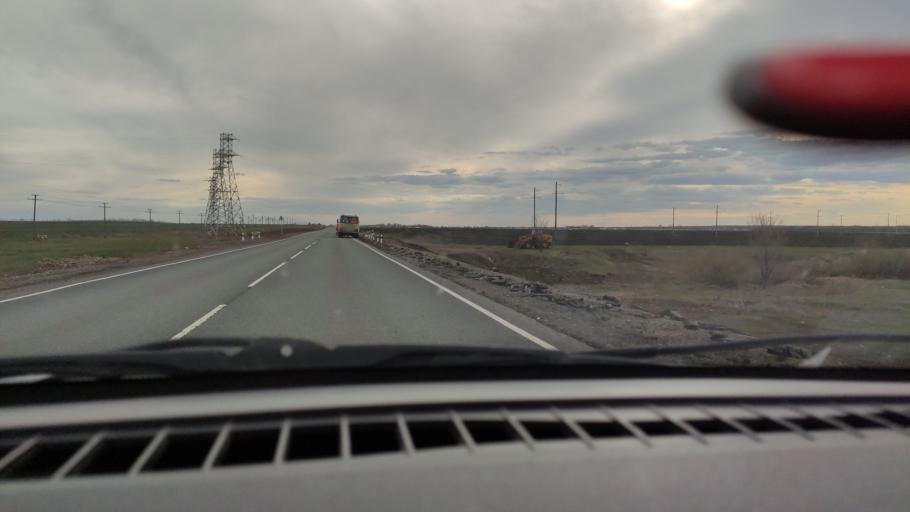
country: RU
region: Bashkortostan
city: Mayachnyy
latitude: 52.3697
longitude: 55.6167
